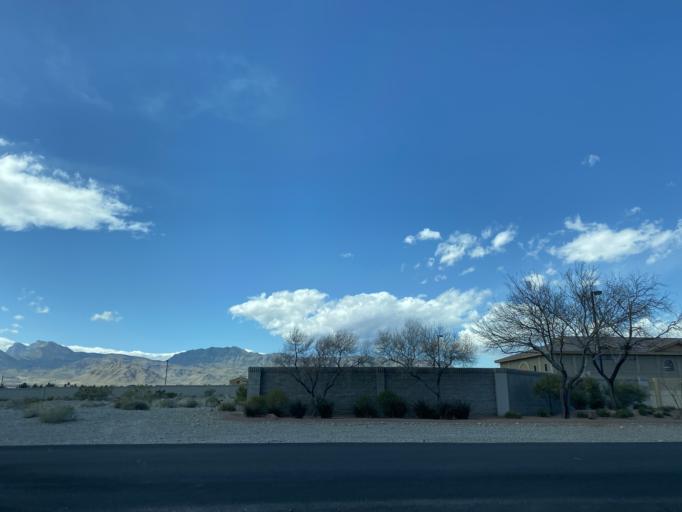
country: US
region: Nevada
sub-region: Clark County
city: Summerlin South
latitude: 36.2719
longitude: -115.2879
